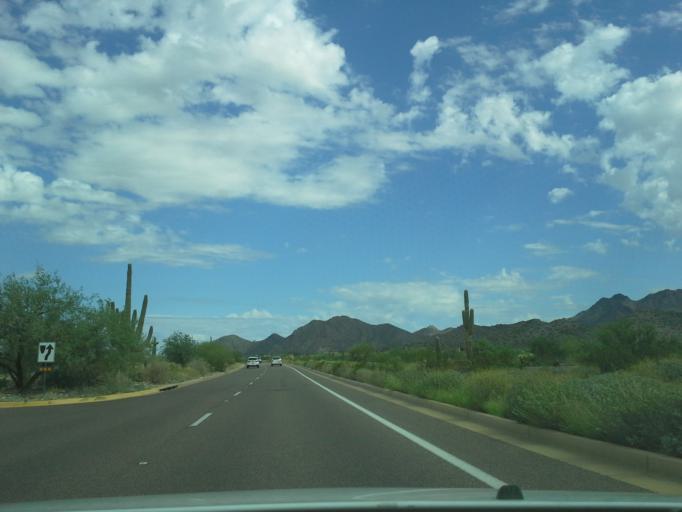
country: US
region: Arizona
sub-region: Maricopa County
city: Paradise Valley
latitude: 33.6418
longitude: -111.8609
